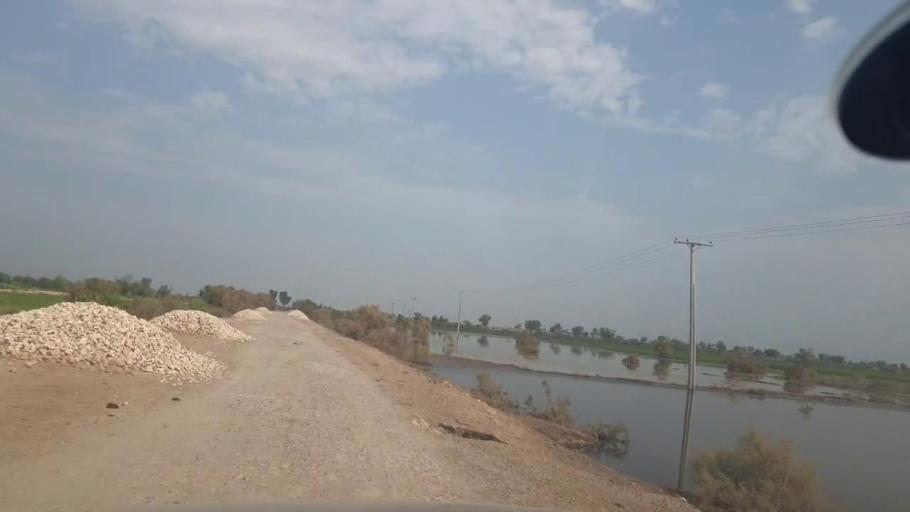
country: PK
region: Balochistan
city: Mehrabpur
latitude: 28.0689
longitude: 68.1025
